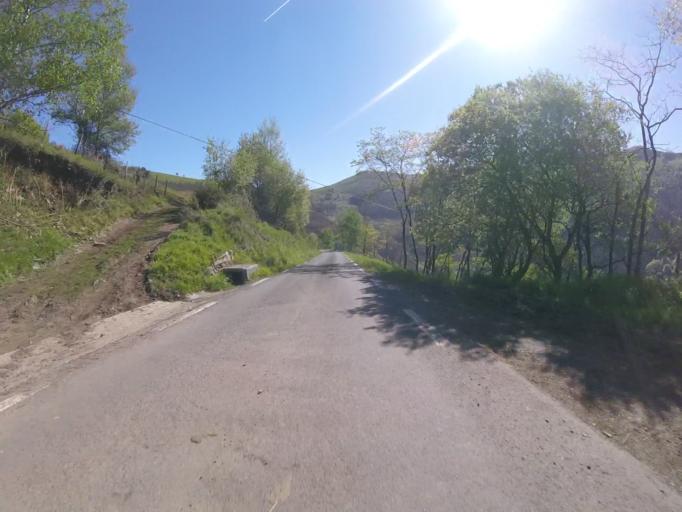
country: ES
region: Basque Country
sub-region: Provincia de Guipuzcoa
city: Errezil
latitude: 43.1889
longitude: -2.2006
